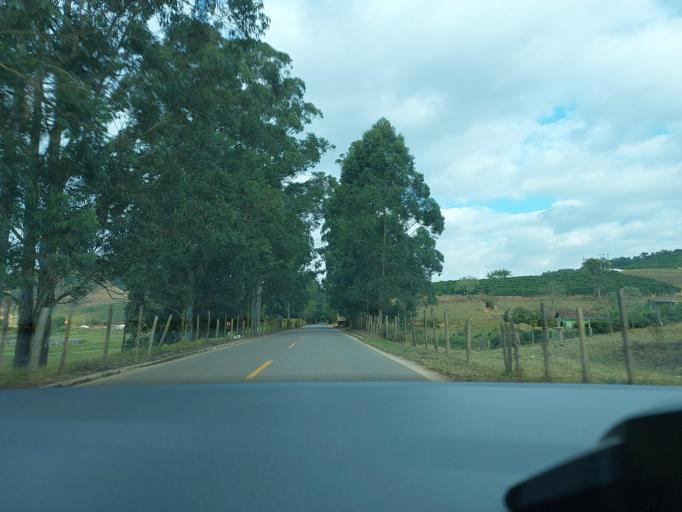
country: BR
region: Minas Gerais
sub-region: Visconde Do Rio Branco
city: Visconde do Rio Branco
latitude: -20.9052
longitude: -42.6495
